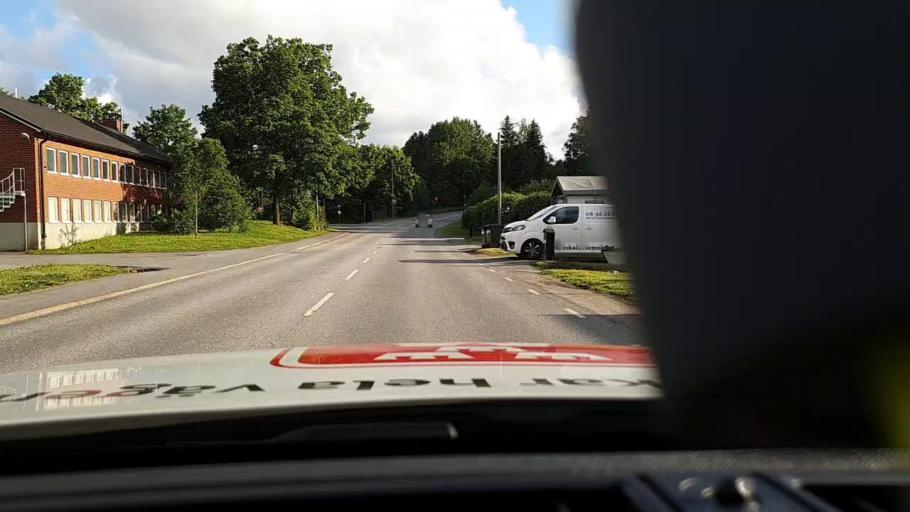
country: SE
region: Stockholm
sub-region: Huddinge Kommun
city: Huddinge
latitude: 59.2587
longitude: 17.9736
